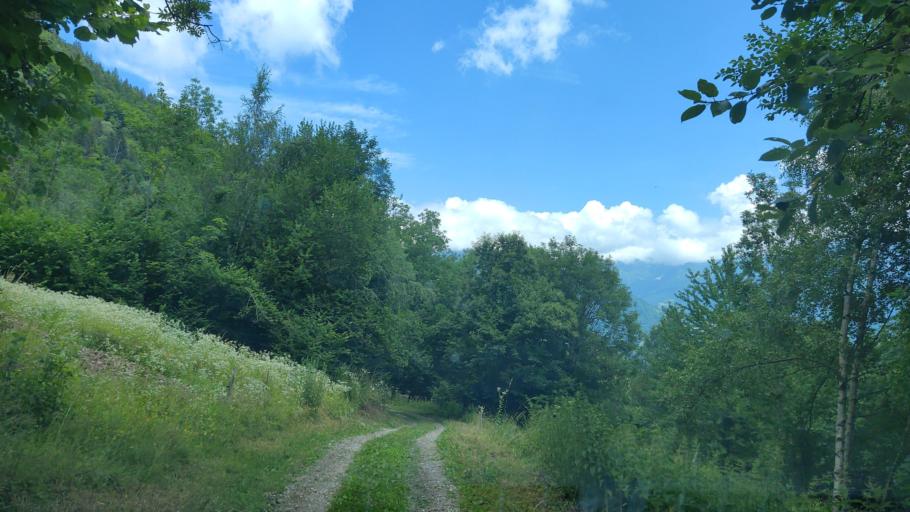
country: FR
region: Rhone-Alpes
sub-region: Departement de la Savoie
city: Aiton
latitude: 45.5110
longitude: 6.2782
